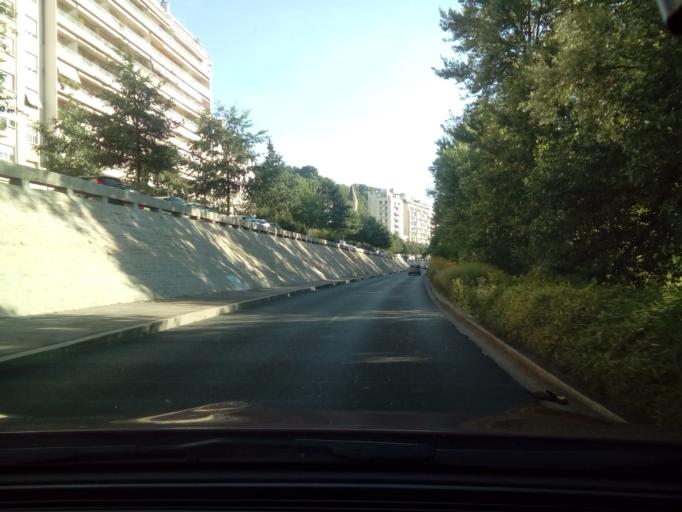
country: FR
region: Rhone-Alpes
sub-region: Departement du Rhone
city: Caluire-et-Cuire
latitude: 45.7831
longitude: 4.8446
